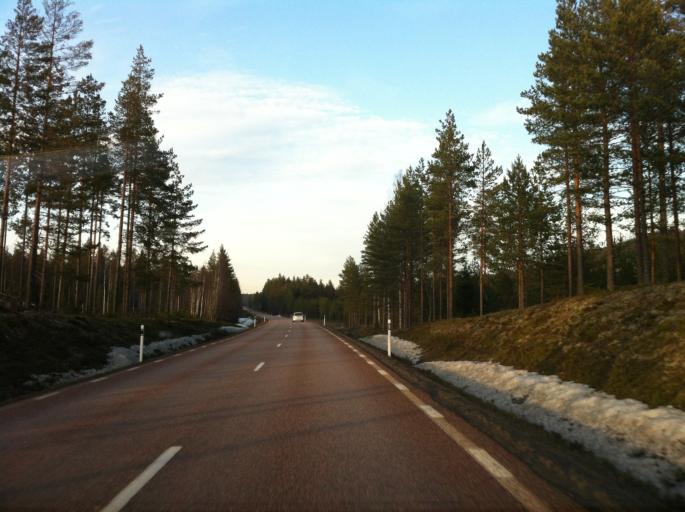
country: SE
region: Dalarna
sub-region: Vansbro Kommun
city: Vansbro
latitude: 60.4060
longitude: 14.2252
